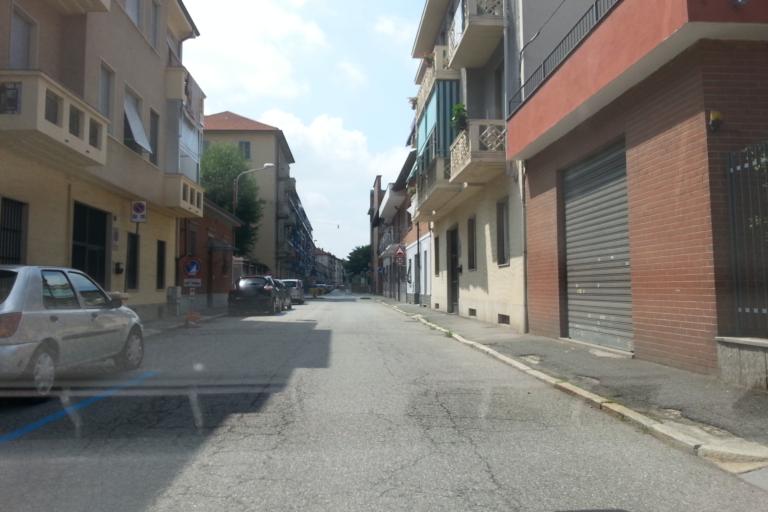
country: IT
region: Piedmont
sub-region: Provincia di Torino
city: Venaria Reale
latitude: 45.1306
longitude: 7.6323
